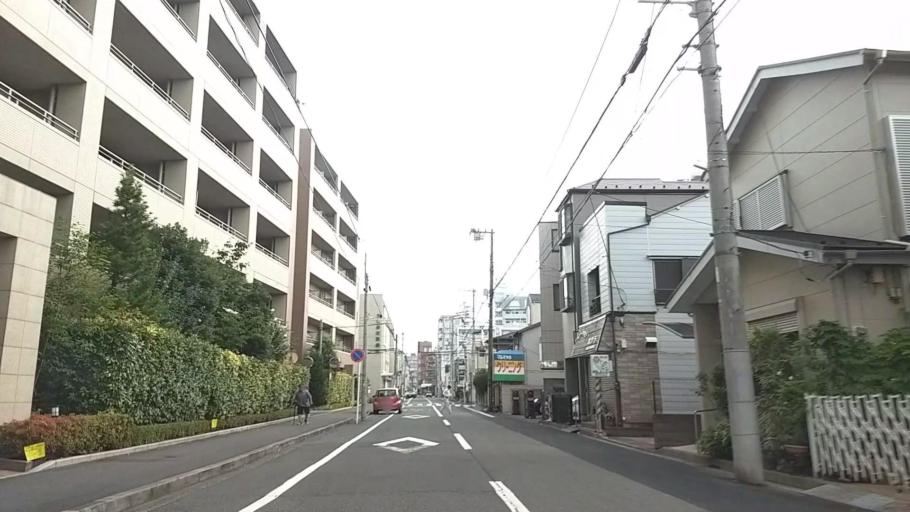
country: JP
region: Kanagawa
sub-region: Kawasaki-shi
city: Kawasaki
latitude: 35.5014
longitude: 139.6795
